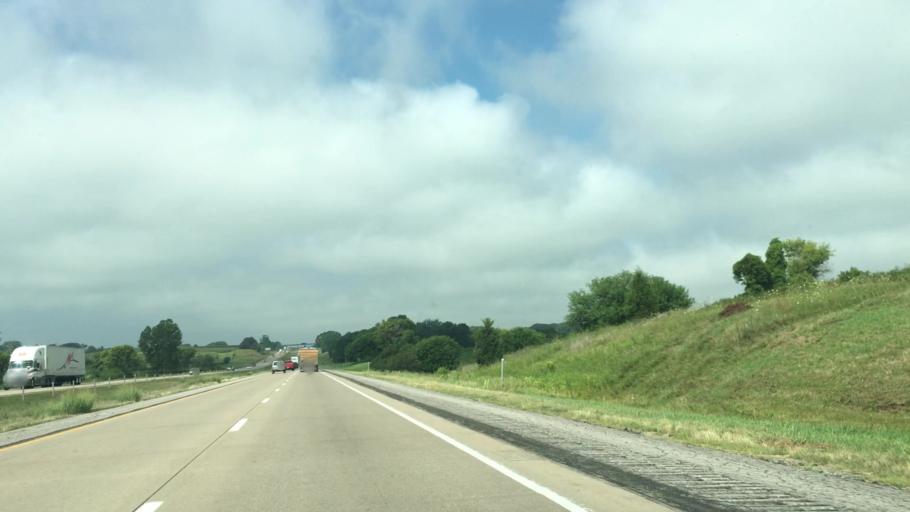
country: US
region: Iowa
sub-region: Cedar County
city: West Branch
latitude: 41.6674
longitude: -91.4045
